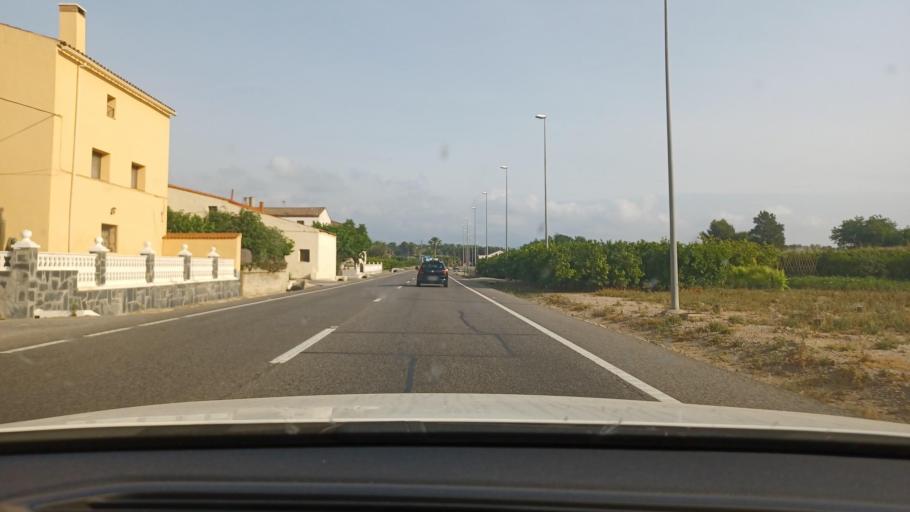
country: ES
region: Catalonia
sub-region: Provincia de Tarragona
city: Tortosa
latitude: 40.7797
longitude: 0.5057
